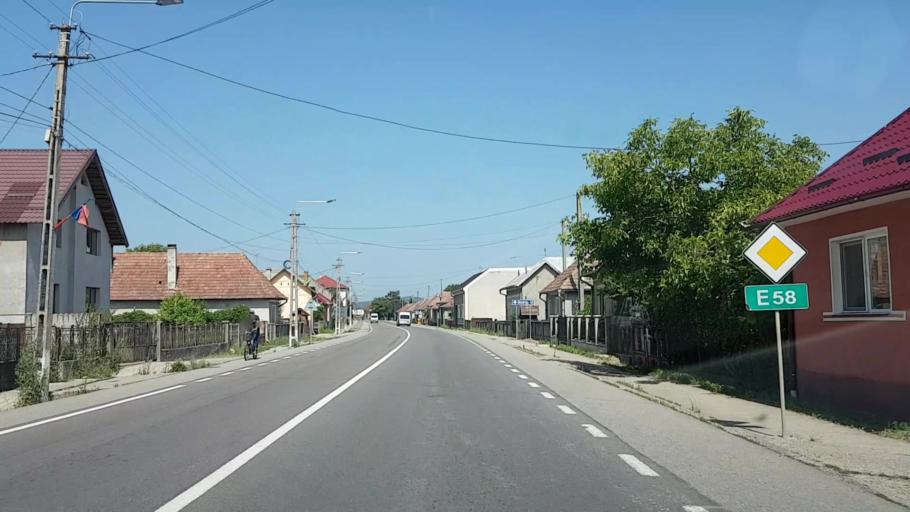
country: RO
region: Bistrita-Nasaud
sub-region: Comuna Petru Rares
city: Reteag
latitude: 47.1918
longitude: 24.0095
